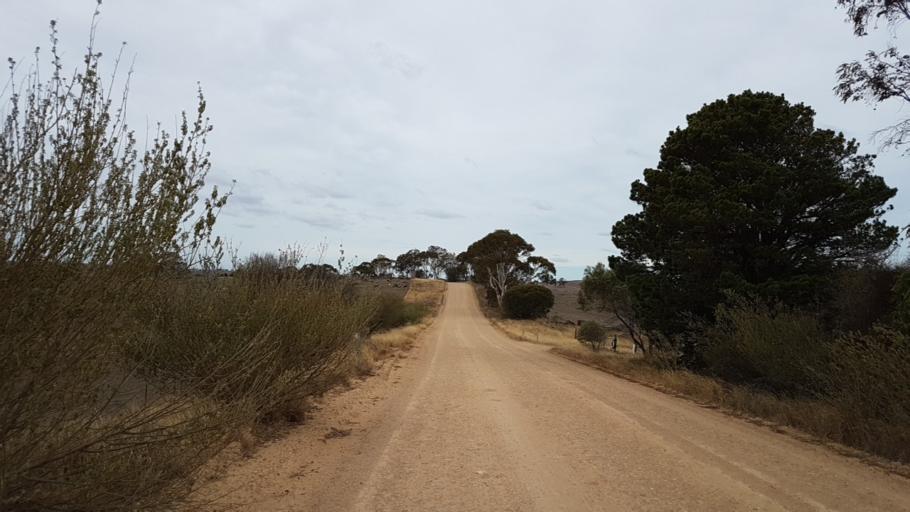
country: AU
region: South Australia
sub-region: Adelaide Hills
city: Birdwood
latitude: -34.8735
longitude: 139.0796
